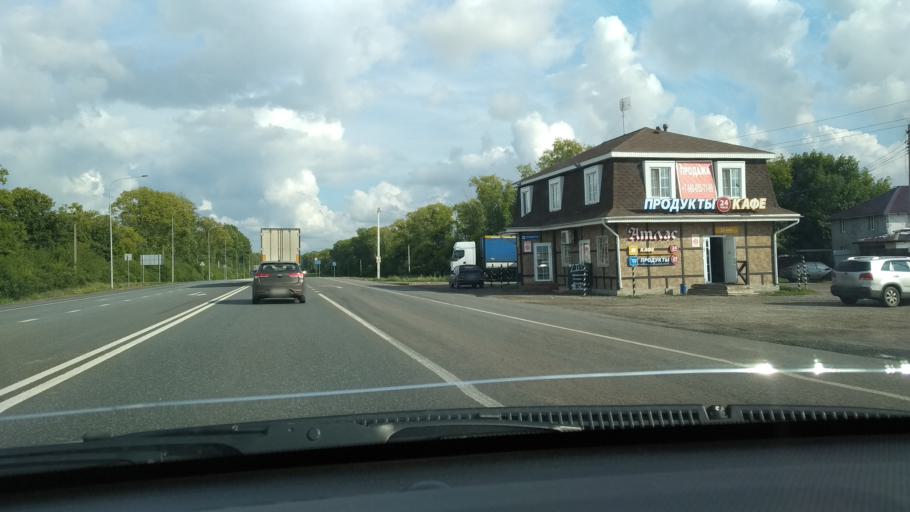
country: RU
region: Tatarstan
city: Stolbishchi
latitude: 55.6557
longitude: 49.3121
